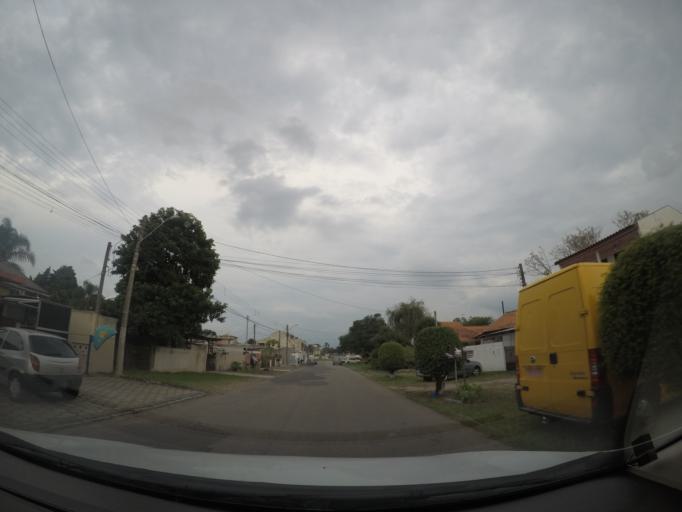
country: BR
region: Parana
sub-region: Sao Jose Dos Pinhais
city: Sao Jose dos Pinhais
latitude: -25.5138
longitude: -49.2293
